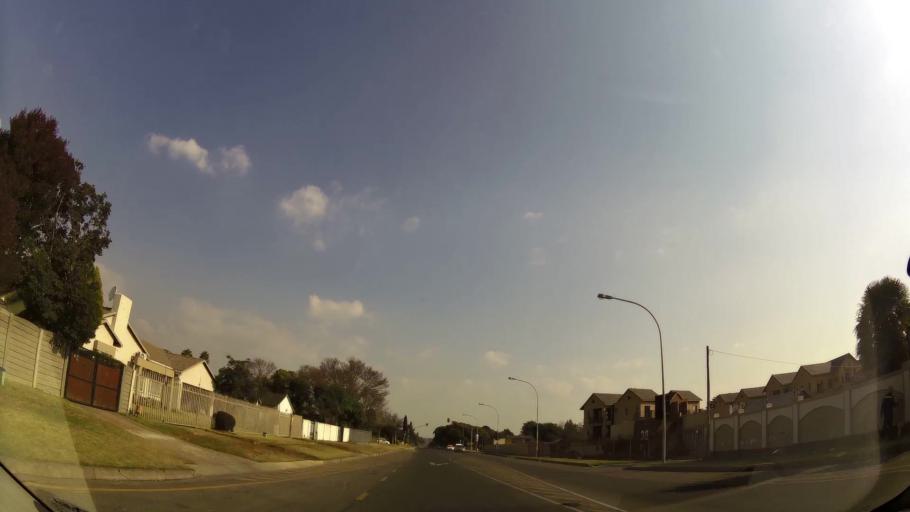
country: ZA
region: Gauteng
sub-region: Ekurhuleni Metropolitan Municipality
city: Benoni
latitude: -26.1520
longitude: 28.2956
